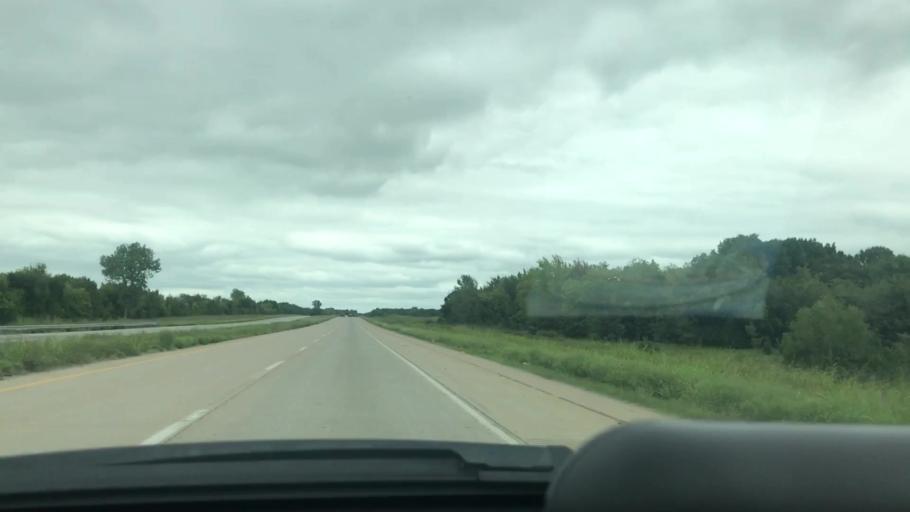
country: US
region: Oklahoma
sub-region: Mayes County
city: Chouteau
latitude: 36.2084
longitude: -95.3408
